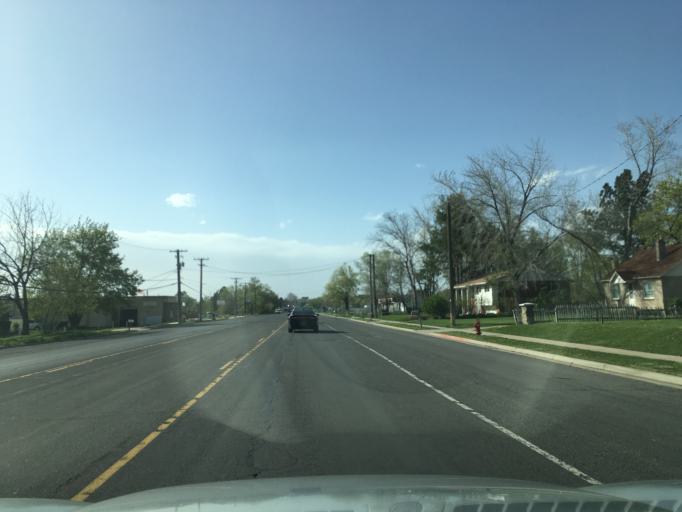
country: US
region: Utah
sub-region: Davis County
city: Kaysville
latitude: 41.0434
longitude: -111.9487
